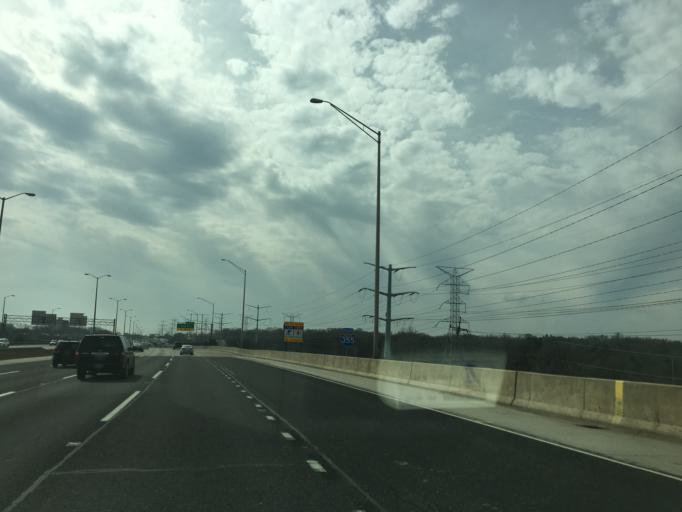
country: US
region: Illinois
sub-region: DuPage County
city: Lisle
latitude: 41.7989
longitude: -88.0571
